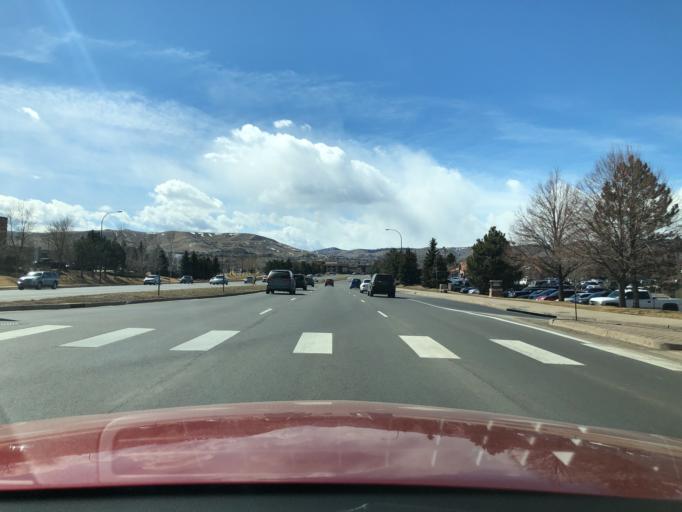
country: US
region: Colorado
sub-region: Jefferson County
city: West Pleasant View
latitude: 39.7351
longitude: -105.1597
